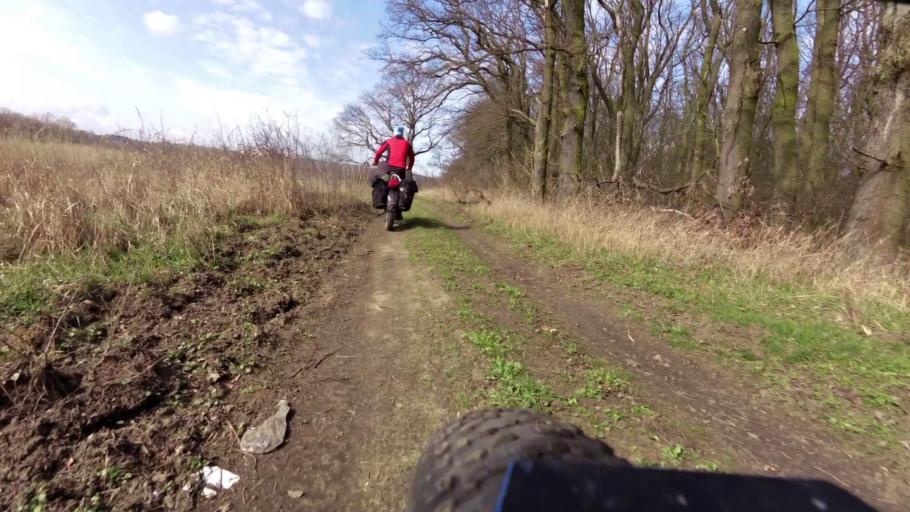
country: PL
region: Lubusz
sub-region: Powiat slubicki
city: Slubice
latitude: 52.3257
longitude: 14.5729
